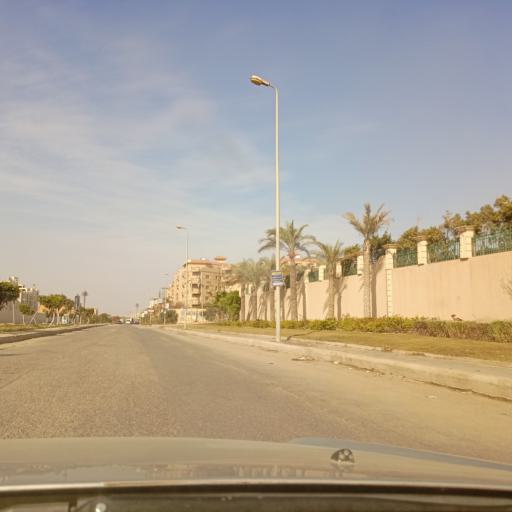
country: EG
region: Muhafazat al Qalyubiyah
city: Al Khankah
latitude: 30.0317
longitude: 31.4851
